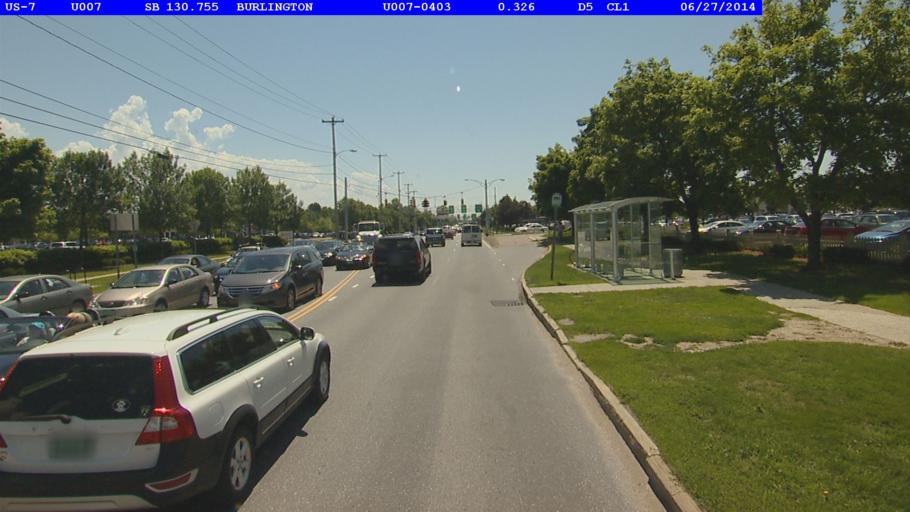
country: US
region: Vermont
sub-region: Chittenden County
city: Burlington
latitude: 44.4505
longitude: -73.2091
